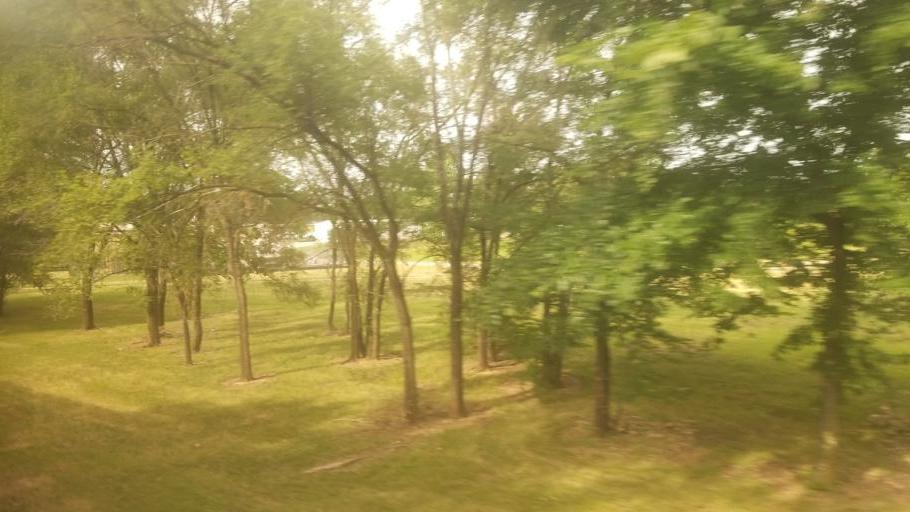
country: US
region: Kansas
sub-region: Douglas County
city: Lawrence
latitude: 38.9821
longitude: -95.2438
